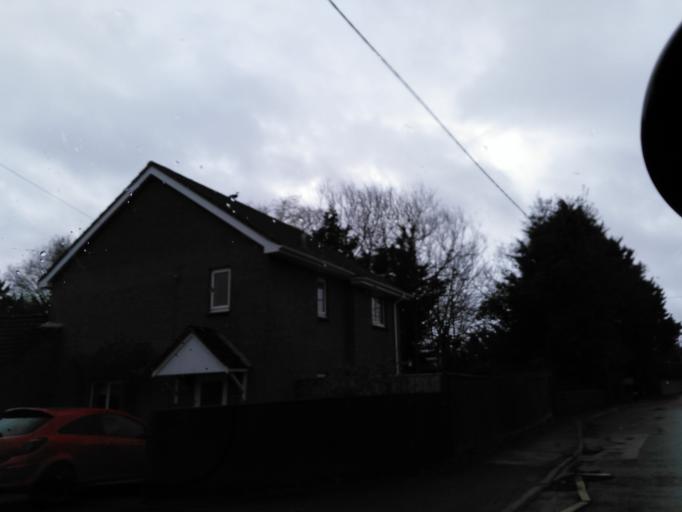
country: GB
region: England
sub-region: Wiltshire
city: Melksham
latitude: 51.3603
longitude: -2.1434
